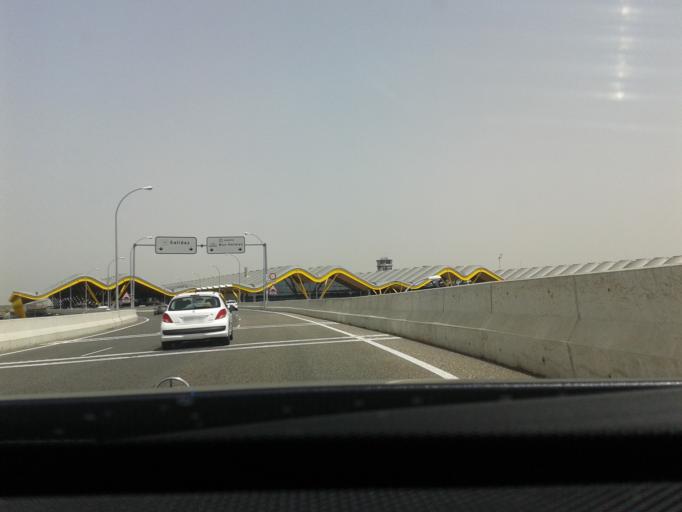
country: ES
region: Madrid
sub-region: Provincia de Madrid
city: Barajas de Madrid
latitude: 40.4874
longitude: -3.5938
